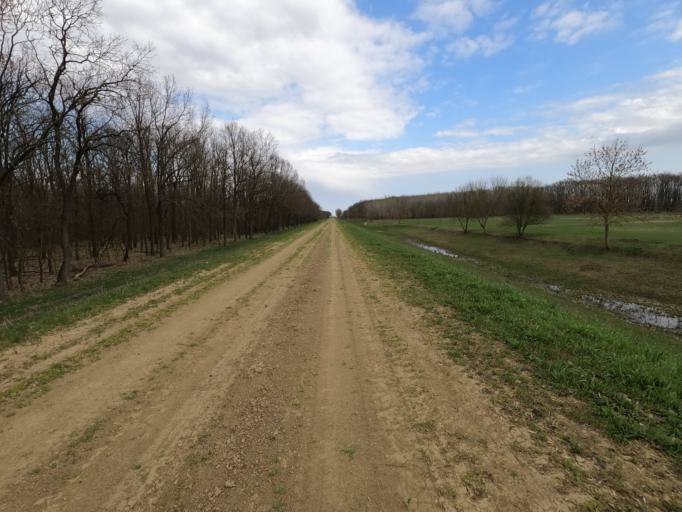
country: HU
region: Jasz-Nagykun-Szolnok
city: Turkeve
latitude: 47.0993
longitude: 20.7937
